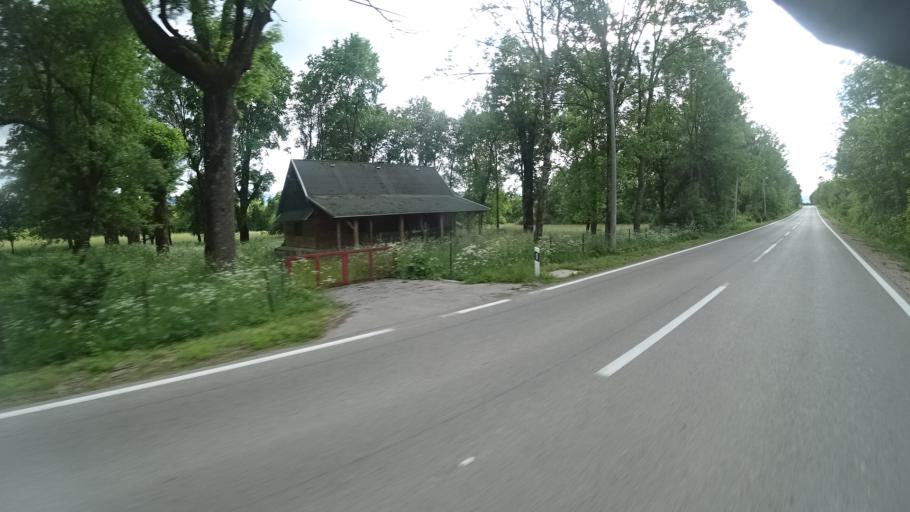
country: HR
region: Licko-Senjska
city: Gospic
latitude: 44.5074
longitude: 15.4412
